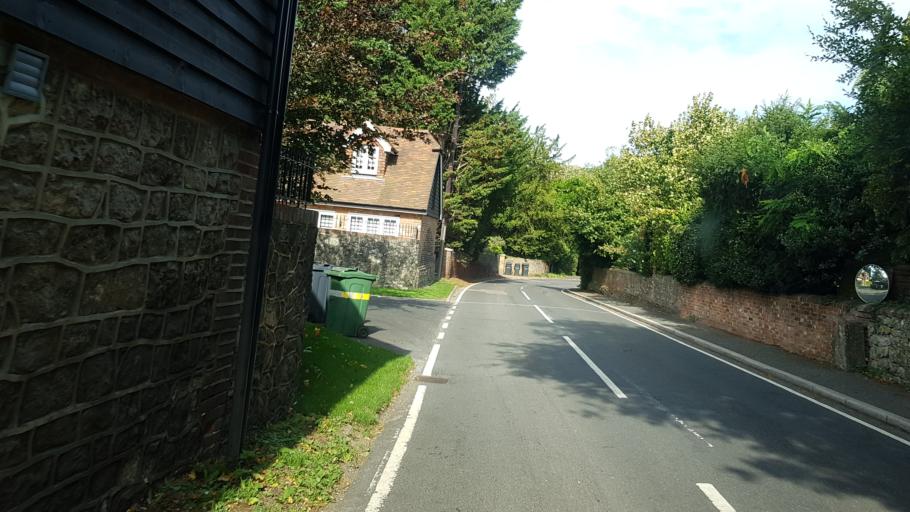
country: GB
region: England
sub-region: Kent
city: Wateringbury
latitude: 51.2495
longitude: 0.4542
